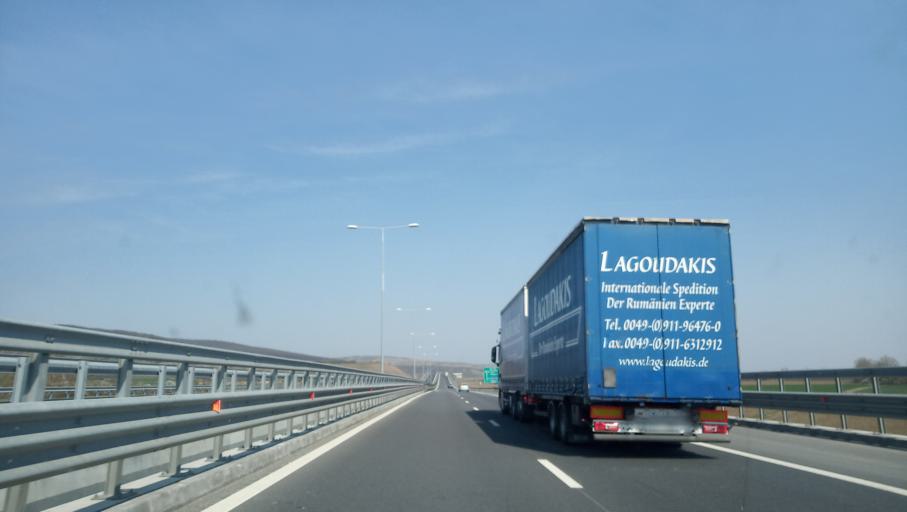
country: RO
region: Alba
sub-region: Comuna Miraslau
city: Miraslau
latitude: 46.3655
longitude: 23.7357
